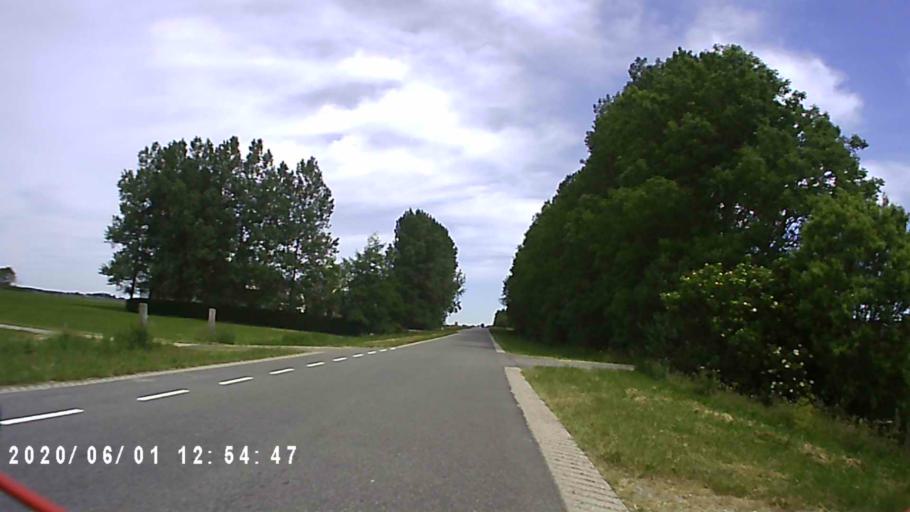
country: NL
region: Friesland
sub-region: Gemeente Franekeradeel
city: Tzum
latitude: 53.1412
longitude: 5.5193
